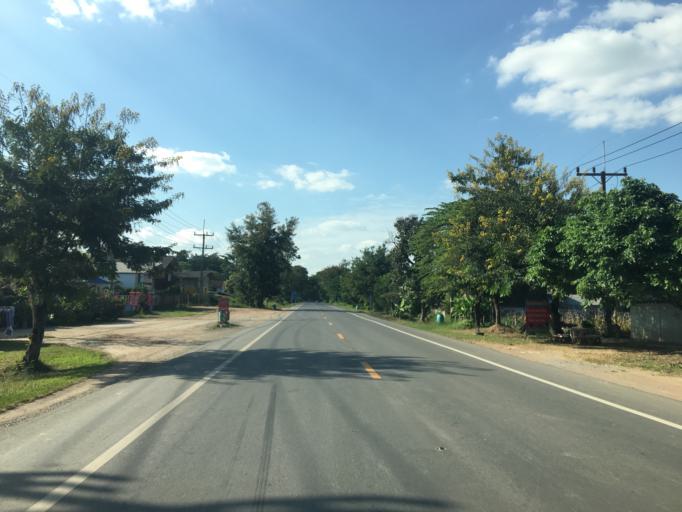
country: TH
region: Phayao
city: Chun
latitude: 19.3458
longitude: 100.1165
